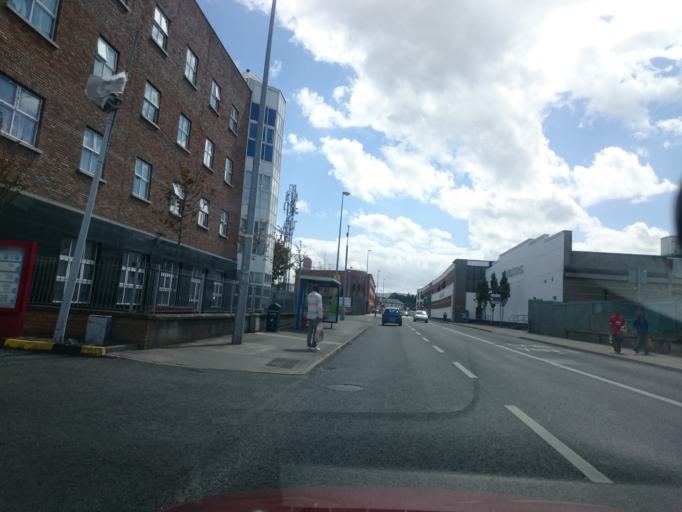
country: IE
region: Leinster
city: Clondalkin
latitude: 53.3256
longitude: -6.3951
